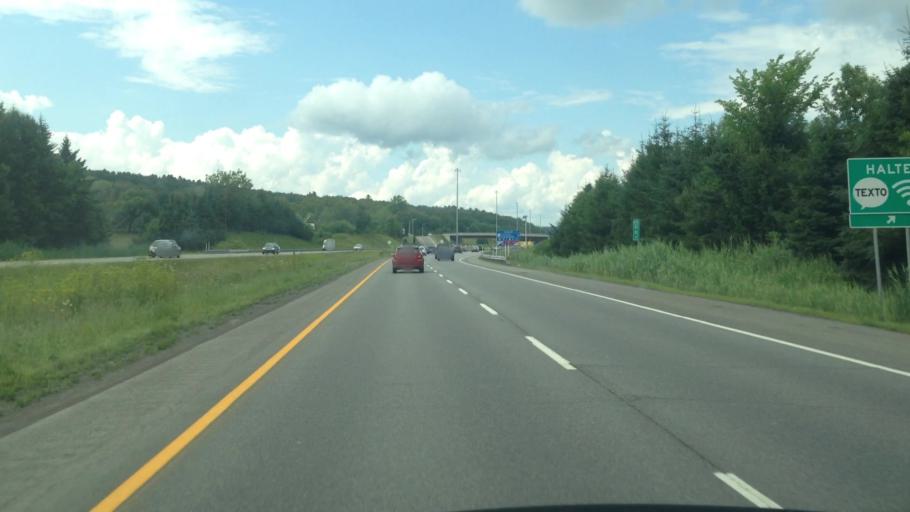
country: CA
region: Quebec
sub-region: Laurentides
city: Prevost
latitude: 45.8364
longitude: -74.0652
